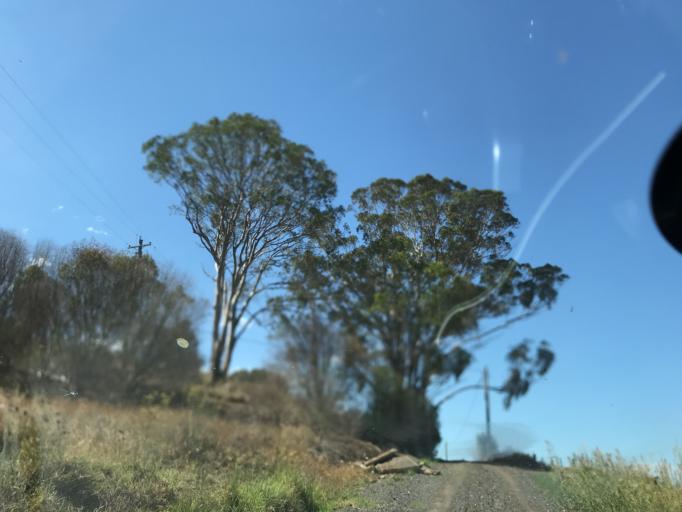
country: AU
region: New South Wales
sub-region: Penrith Municipality
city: Kingswood Park
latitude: -33.7933
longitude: 150.7375
